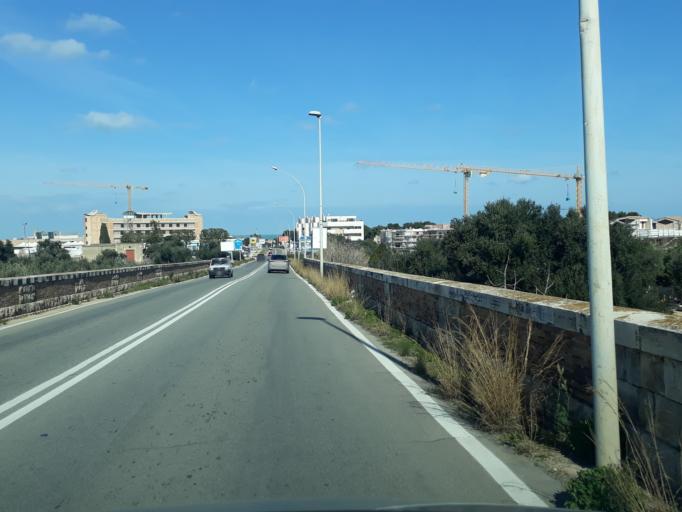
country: IT
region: Apulia
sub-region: Provincia di Bari
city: Monopoli
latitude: 40.9580
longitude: 17.2826
